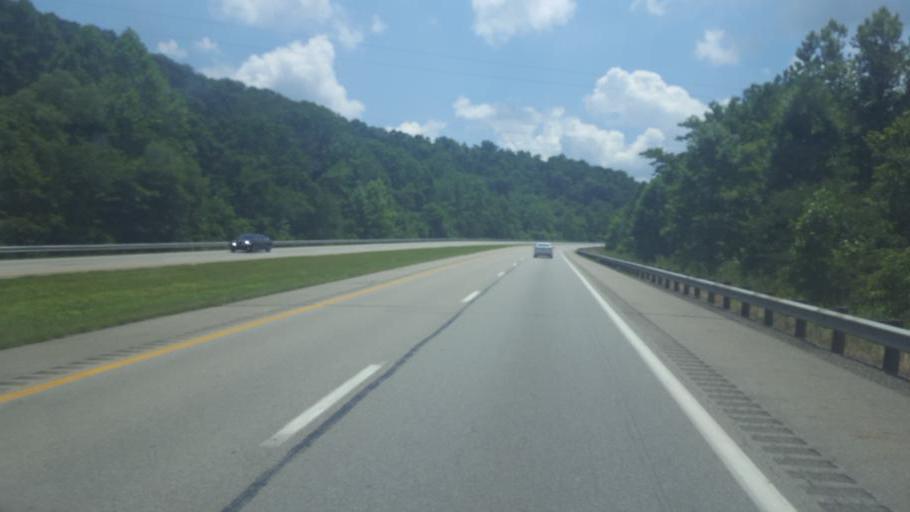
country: US
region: Ohio
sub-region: Jackson County
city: Jackson
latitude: 39.1531
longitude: -82.7311
